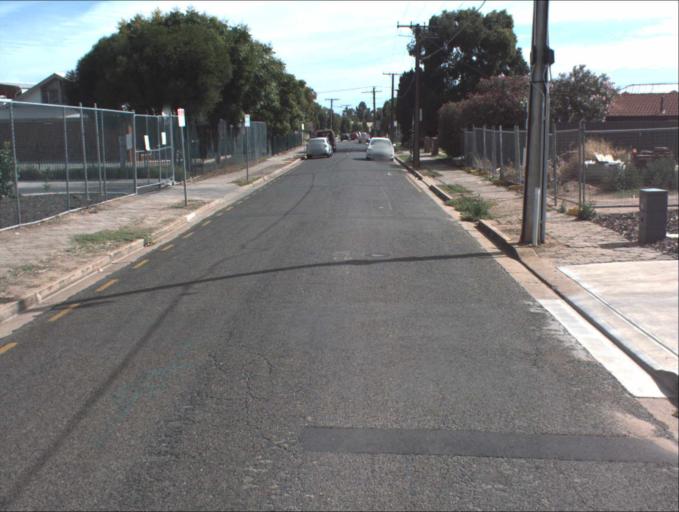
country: AU
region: South Australia
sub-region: Port Adelaide Enfield
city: Klemzig
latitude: -34.8679
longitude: 138.6432
